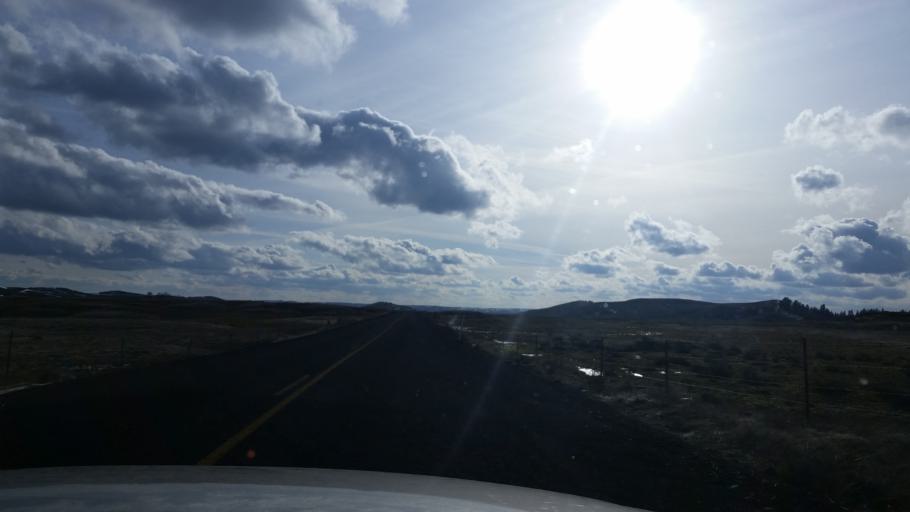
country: US
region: Washington
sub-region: Spokane County
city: Cheney
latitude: 47.3120
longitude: -117.6157
